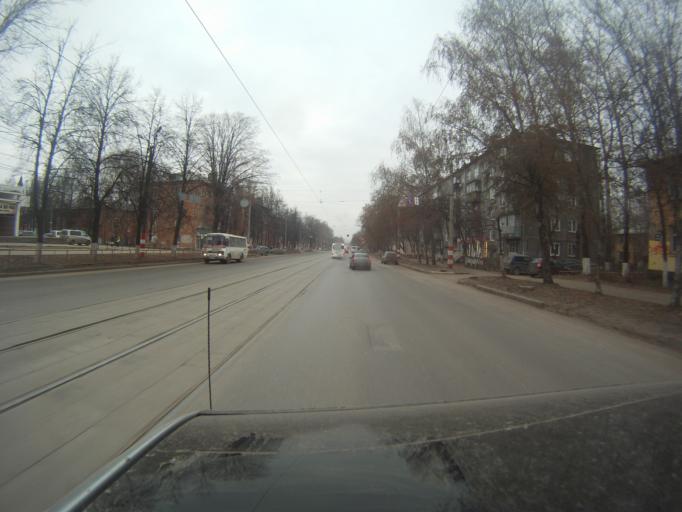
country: RU
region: Nizjnij Novgorod
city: Nizhniy Novgorod
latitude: 56.2920
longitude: 44.0063
